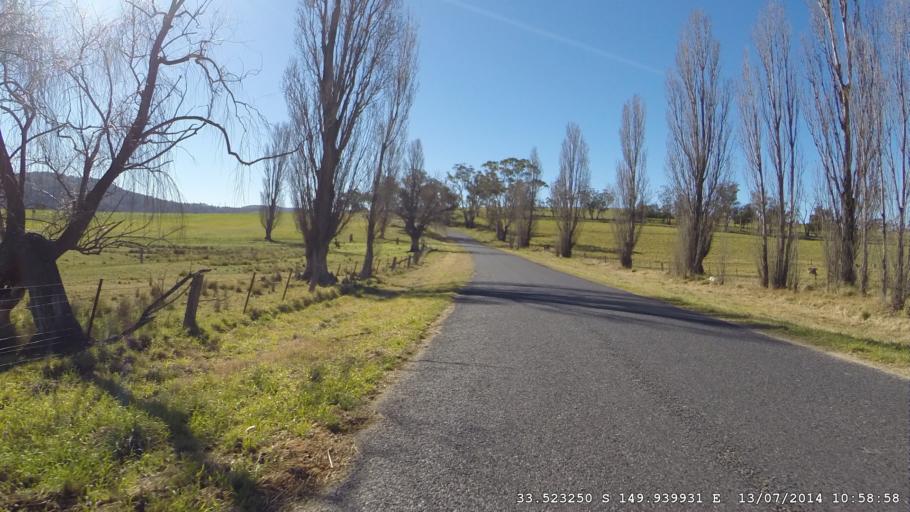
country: AU
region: New South Wales
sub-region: Lithgow
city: Portland
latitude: -33.5233
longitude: 149.9399
